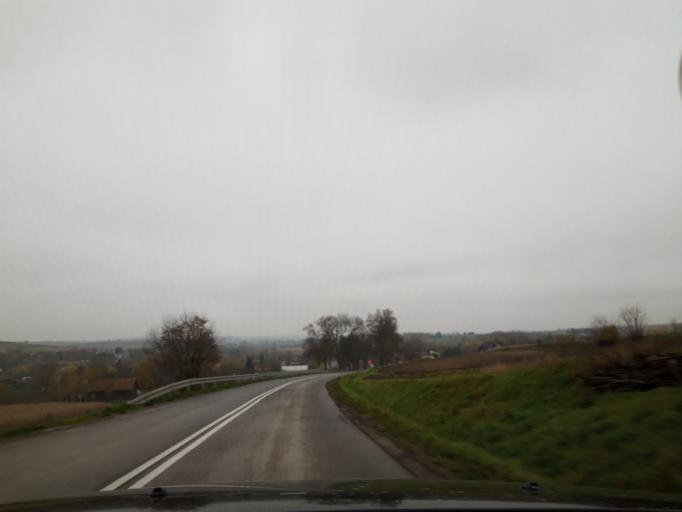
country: PL
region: Swietokrzyskie
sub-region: Powiat pinczowski
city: Dzialoszyce
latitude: 50.3571
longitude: 20.3592
